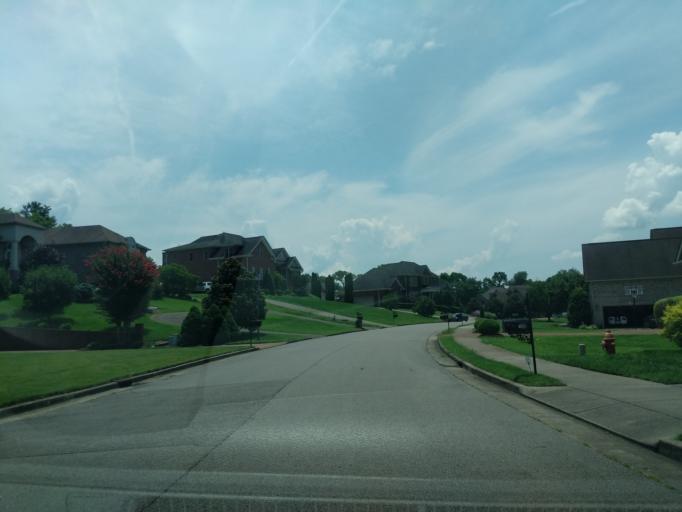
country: US
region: Tennessee
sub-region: Davidson County
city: Lakewood
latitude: 36.2303
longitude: -86.6281
